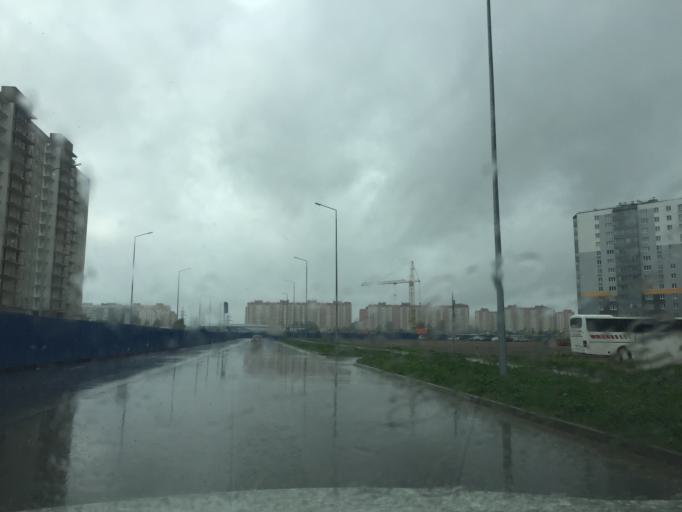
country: RU
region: St.-Petersburg
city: Gorelovo
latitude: 59.7871
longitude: 30.1660
